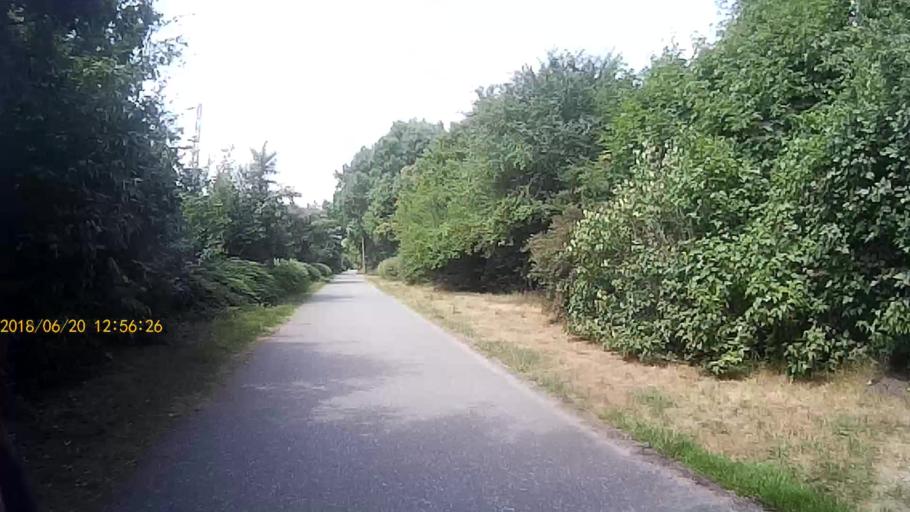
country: DE
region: Lower Saxony
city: Neu Wulmstorf
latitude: 53.4738
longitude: 9.8659
